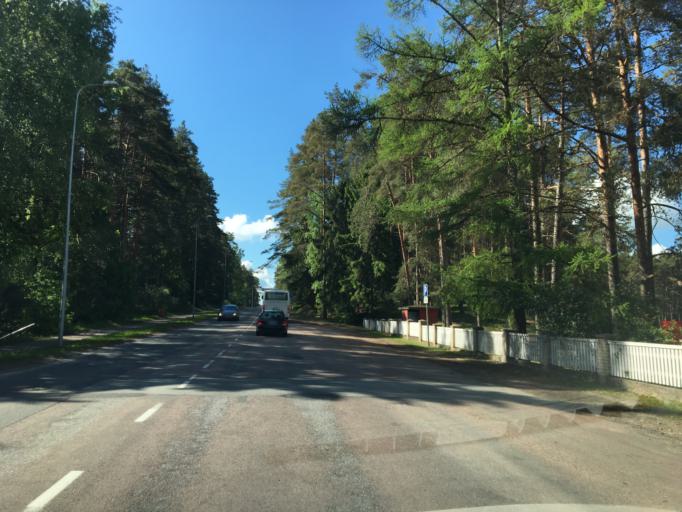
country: EE
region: Tartu
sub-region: Elva linn
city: Elva
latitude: 58.2297
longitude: 26.4074
